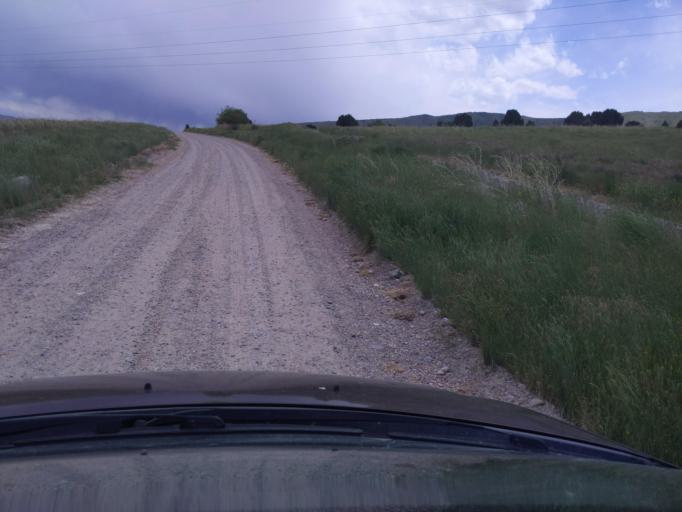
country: US
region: Idaho
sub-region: Bannock County
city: Pocatello
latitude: 42.8472
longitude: -112.4600
